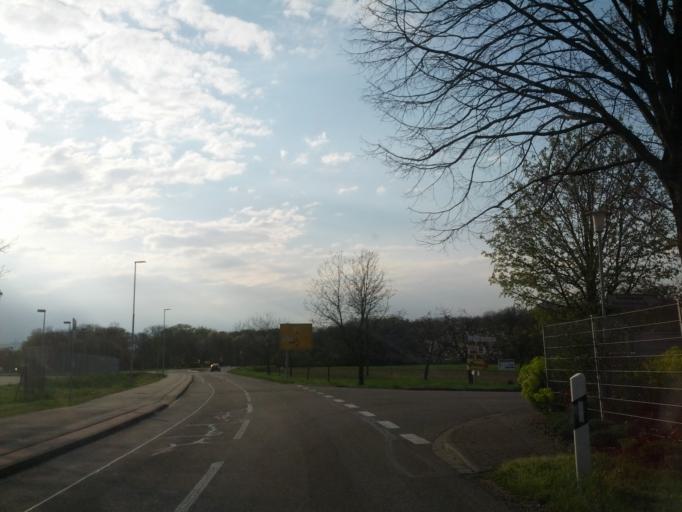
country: DE
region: Baden-Wuerttemberg
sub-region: Freiburg Region
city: Teningen
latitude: 48.0860
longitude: 7.8092
